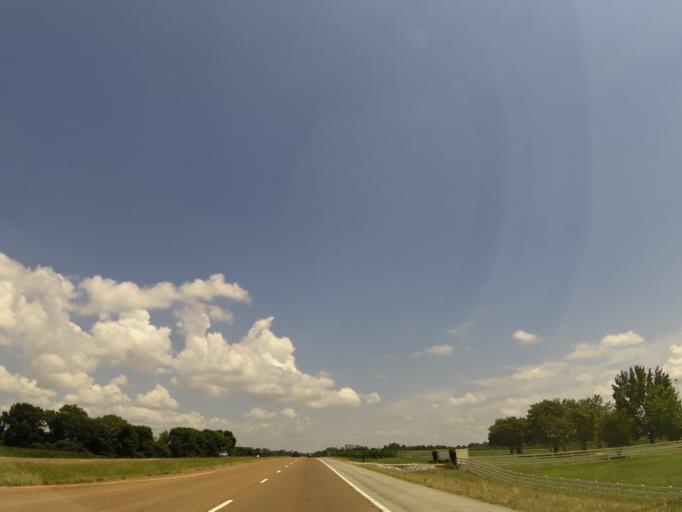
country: US
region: Tennessee
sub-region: Lauderdale County
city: Halls
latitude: 35.9497
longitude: -89.3112
